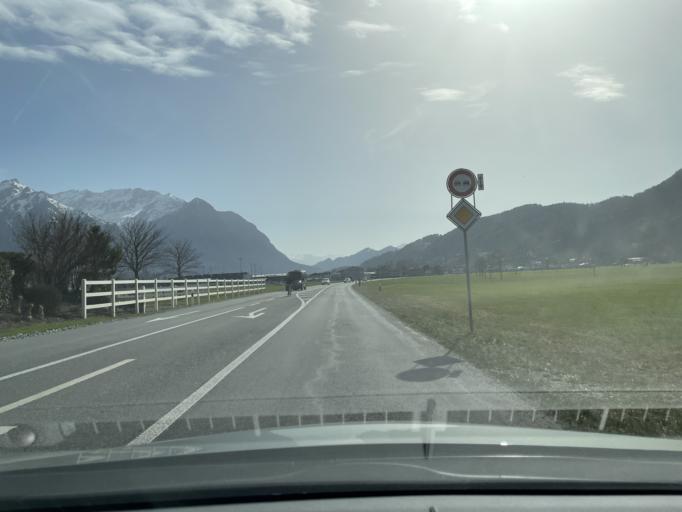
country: CH
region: Saint Gallen
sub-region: Wahlkreis Werdenberg
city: Sevelen
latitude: 47.1353
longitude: 9.4859
